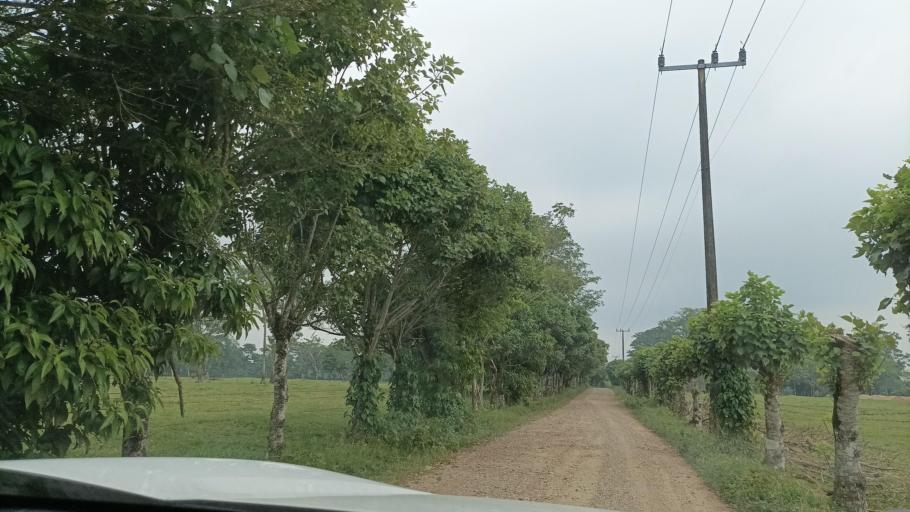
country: MX
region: Veracruz
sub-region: Uxpanapa
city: Poblado 10
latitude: 17.5480
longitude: -94.2302
